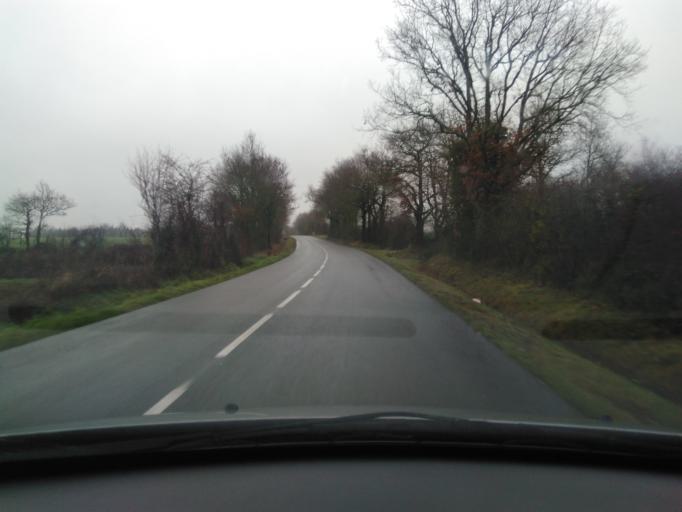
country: FR
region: Pays de la Loire
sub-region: Departement de la Vendee
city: La Chaize-le-Vicomte
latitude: 46.6880
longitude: -1.3044
